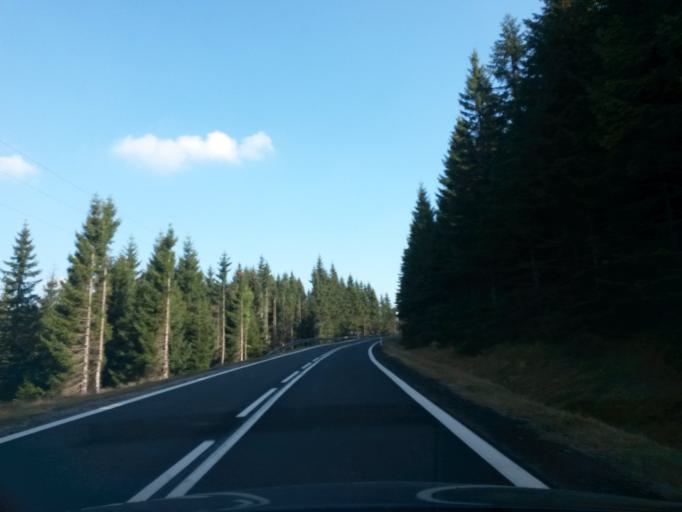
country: CZ
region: Liberecky
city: Harrachov
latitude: 50.8248
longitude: 15.4460
